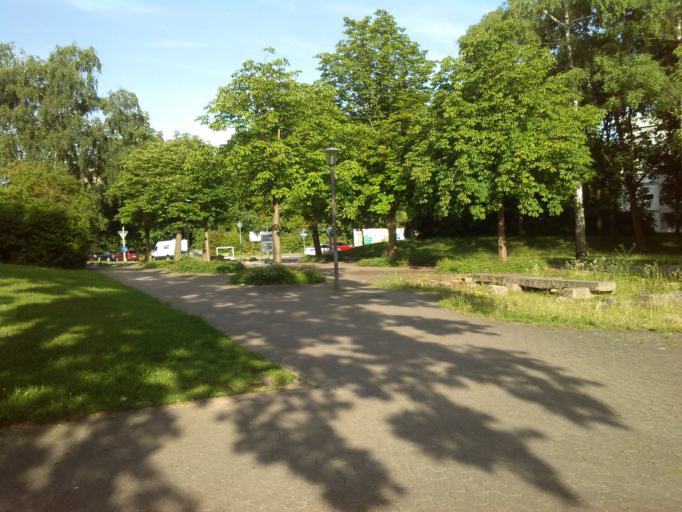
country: DE
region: Bavaria
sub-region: Regierungsbezirk Mittelfranken
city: Wendelstein
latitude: 49.4007
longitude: 11.1399
